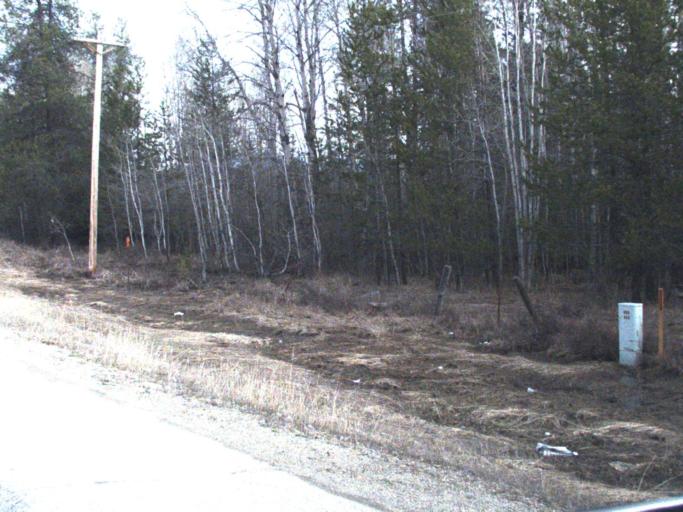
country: US
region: Washington
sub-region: Pend Oreille County
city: Newport
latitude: 48.2733
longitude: -117.2626
